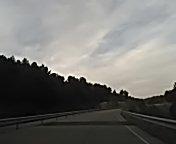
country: ES
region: Castille and Leon
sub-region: Provincia de Soria
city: San Leonardo de Yague
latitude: 41.8304
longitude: -3.0850
